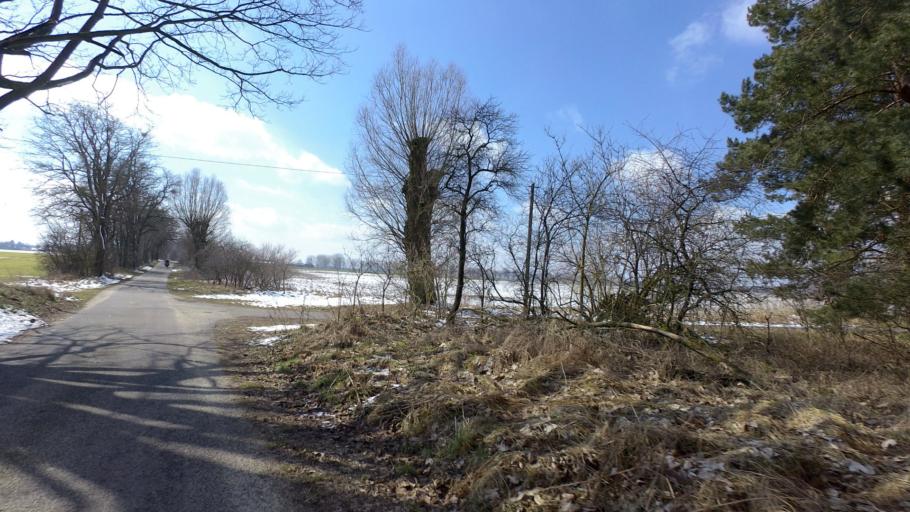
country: DE
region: Brandenburg
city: Werftpfuhl
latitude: 52.7033
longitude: 13.7836
